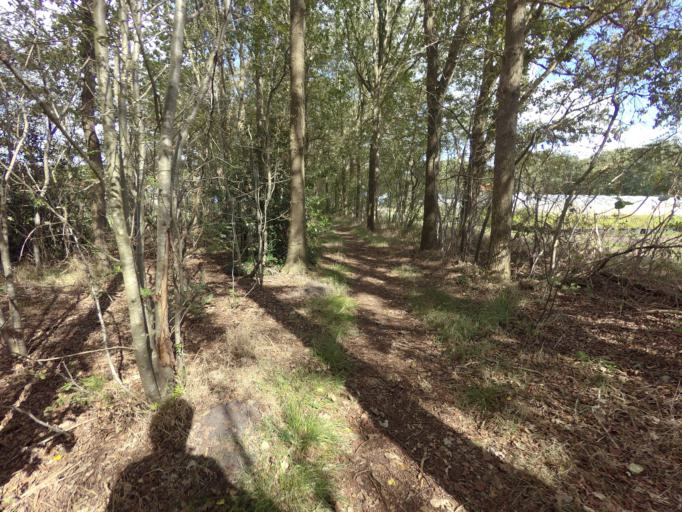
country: NL
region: Friesland
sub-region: Gemeente Weststellingwerf
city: Noordwolde
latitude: 52.9582
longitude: 6.2054
